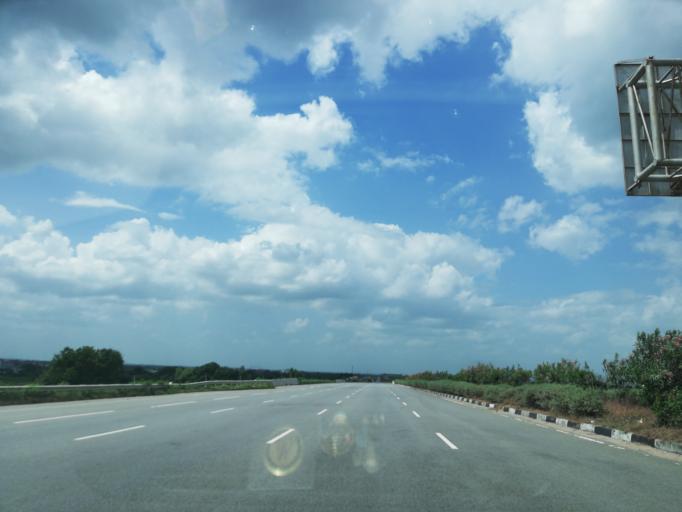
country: IN
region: Telangana
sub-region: Medak
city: Serilingampalle
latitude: 17.4709
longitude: 78.2483
